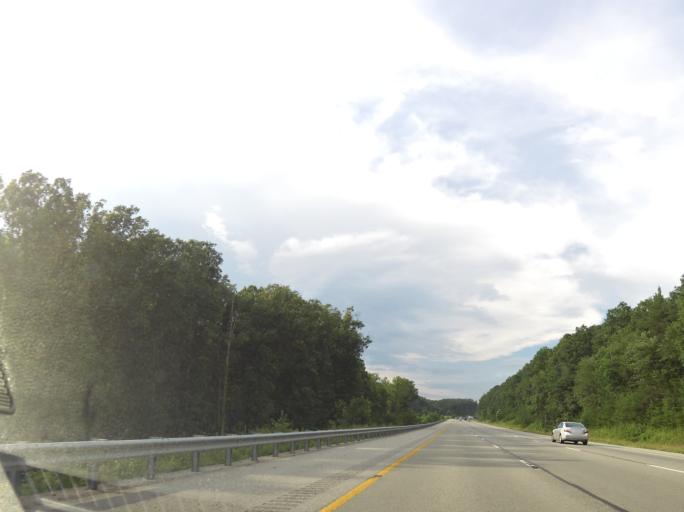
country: US
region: Kentucky
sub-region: Madison County
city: Berea
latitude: 37.5276
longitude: -84.3191
